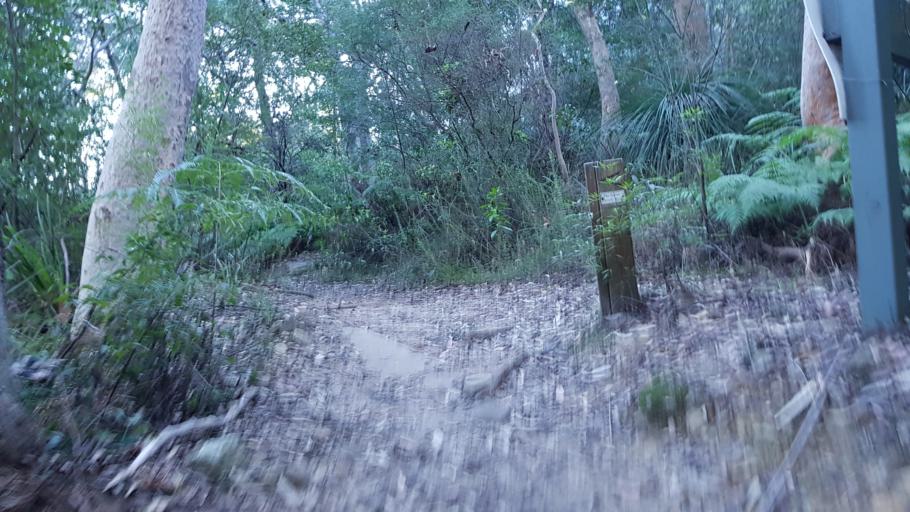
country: AU
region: New South Wales
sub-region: Lane Cove
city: Lane Cove West
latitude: -33.7984
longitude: 151.1469
